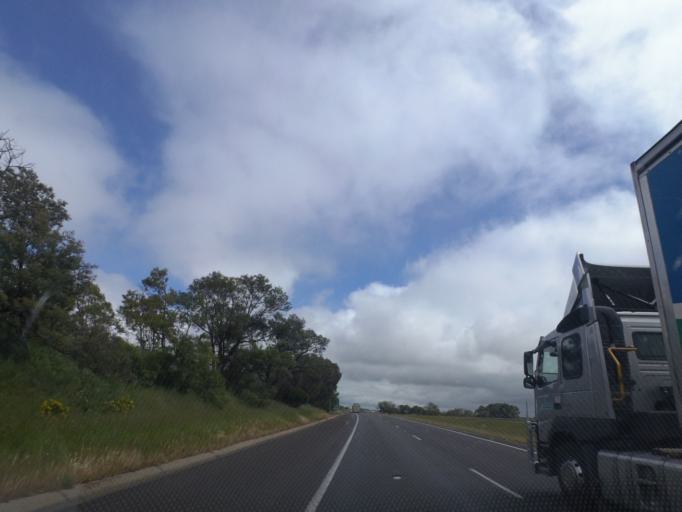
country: AU
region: Victoria
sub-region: Ballarat North
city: Soldiers Hill
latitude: -37.5209
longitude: 143.8540
